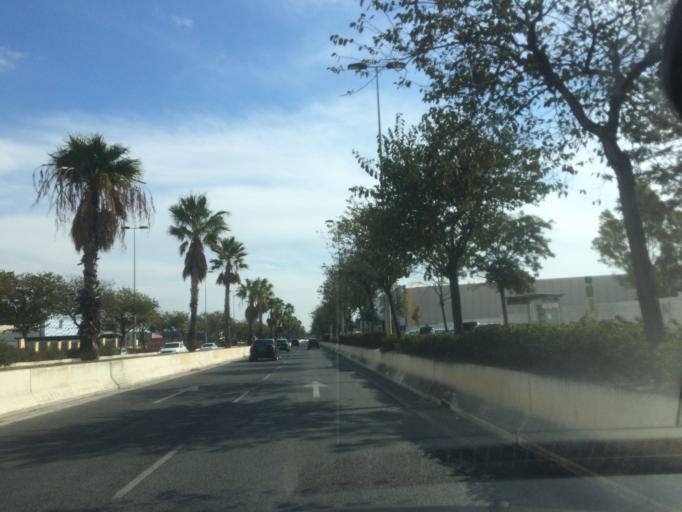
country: ES
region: Andalusia
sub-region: Provincia de Malaga
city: Torremolinos
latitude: 36.6605
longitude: -4.4994
